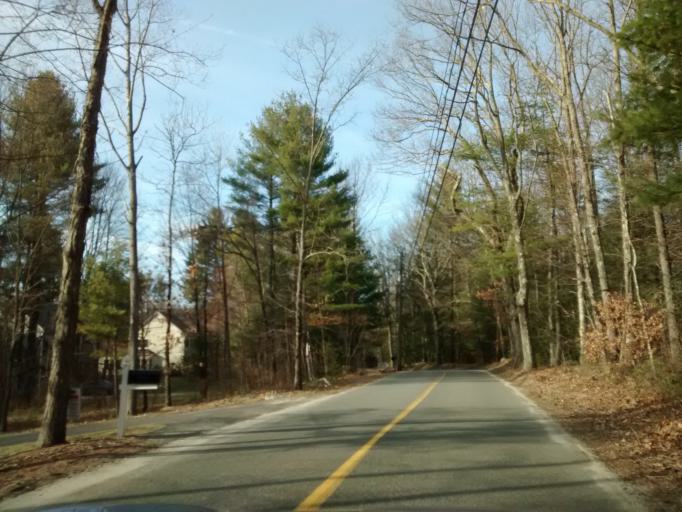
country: US
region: Massachusetts
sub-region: Worcester County
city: Southbridge
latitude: 42.1171
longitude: -72.0208
